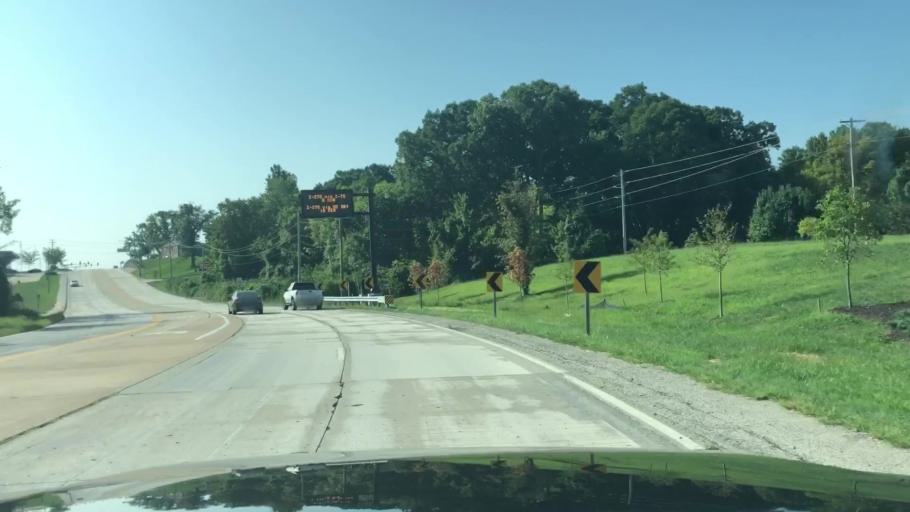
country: US
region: Missouri
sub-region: Saint Charles County
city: Saint Charles
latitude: 38.7720
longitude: -90.5267
